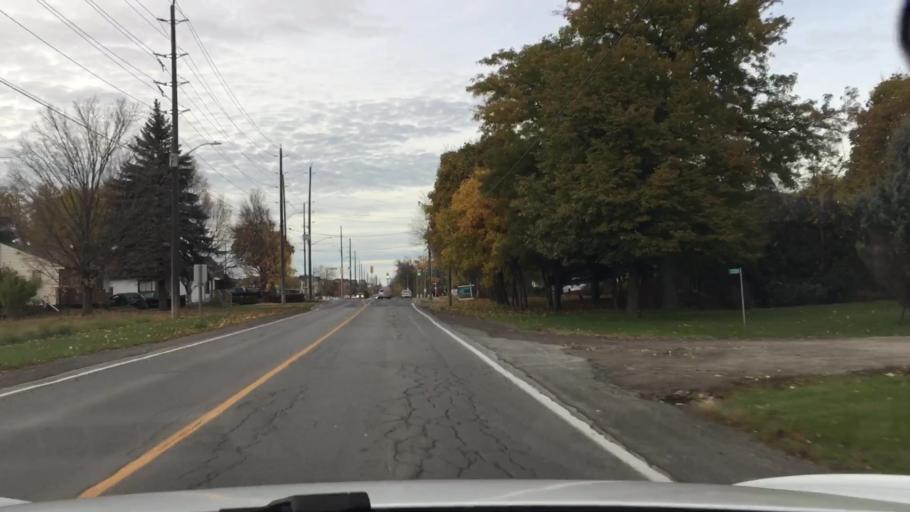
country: CA
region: Ontario
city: Oshawa
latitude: 43.9424
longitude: -78.8291
